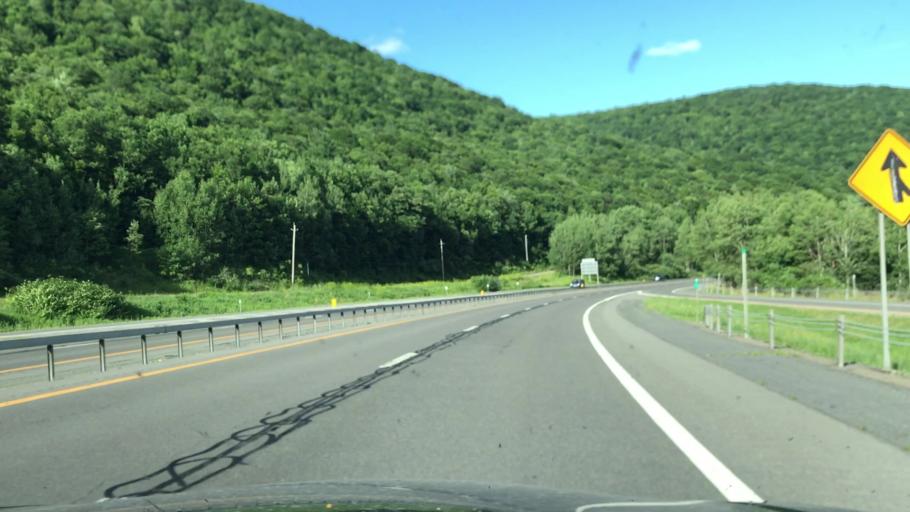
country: US
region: New York
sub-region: Delaware County
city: Hancock
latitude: 41.9662
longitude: -75.2586
